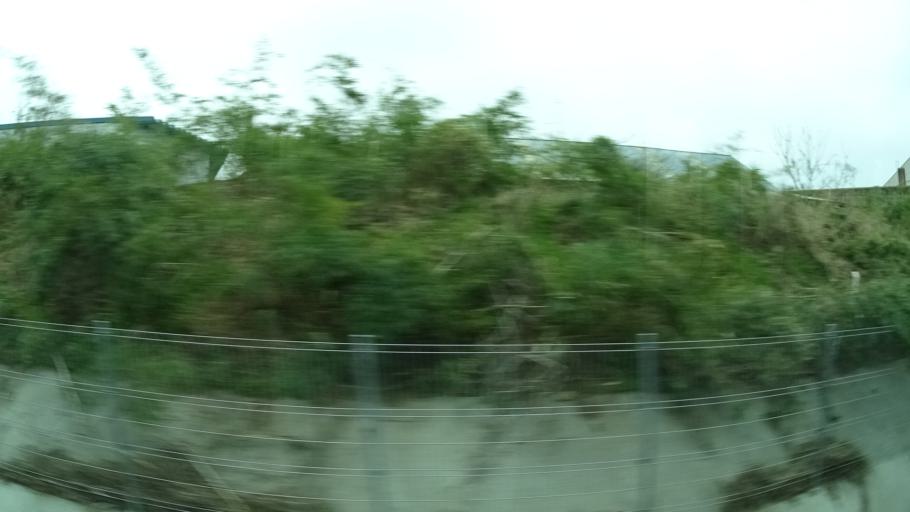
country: JP
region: Fukushima
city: Namie
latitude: 37.4046
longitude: 140.9848
